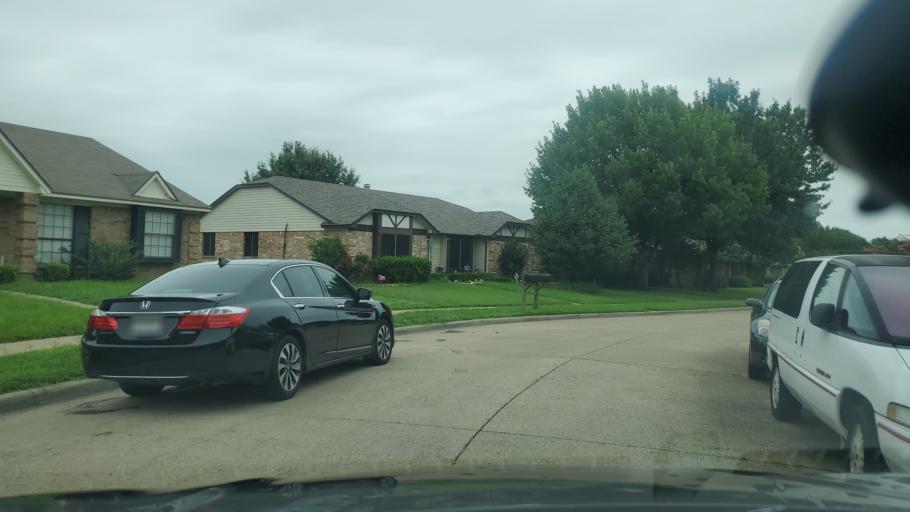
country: US
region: Texas
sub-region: Dallas County
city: Garland
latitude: 32.9404
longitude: -96.6270
